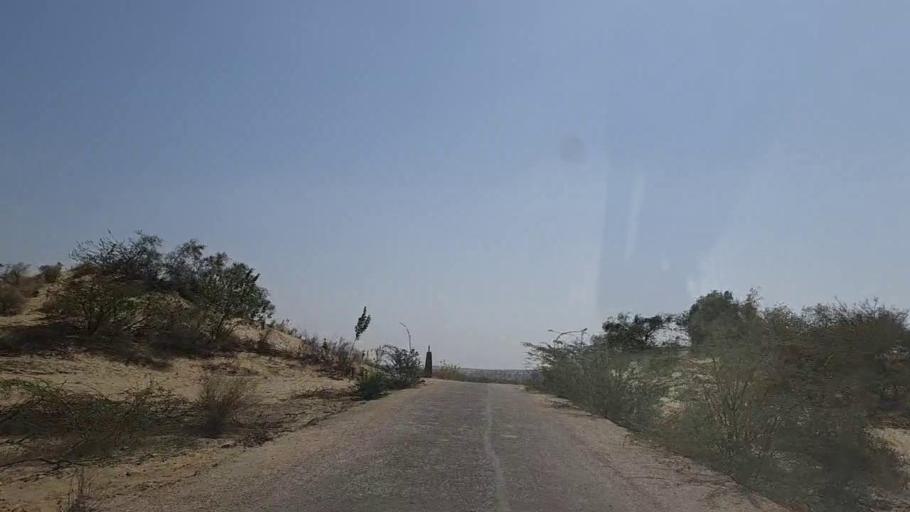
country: PK
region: Sindh
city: Diplo
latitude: 24.5003
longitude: 69.4289
